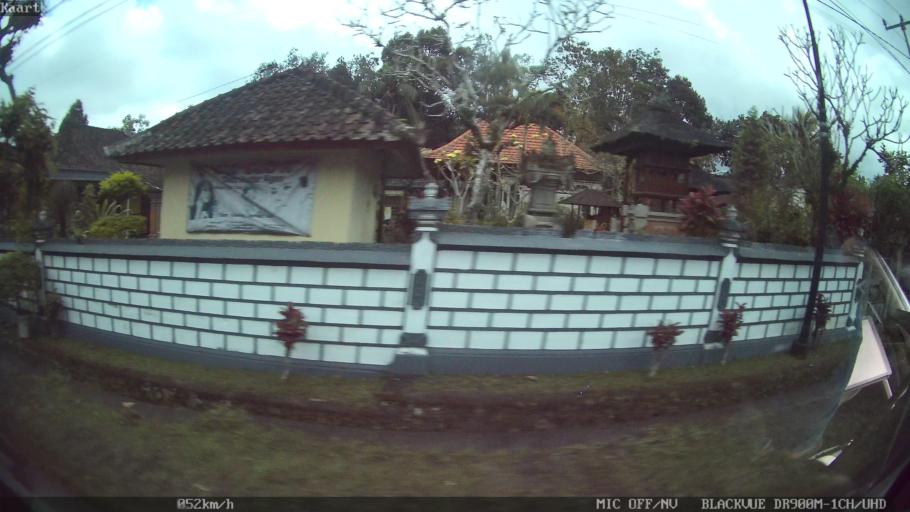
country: ID
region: Bali
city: Banjar Kubu
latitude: -8.3962
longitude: 115.4199
